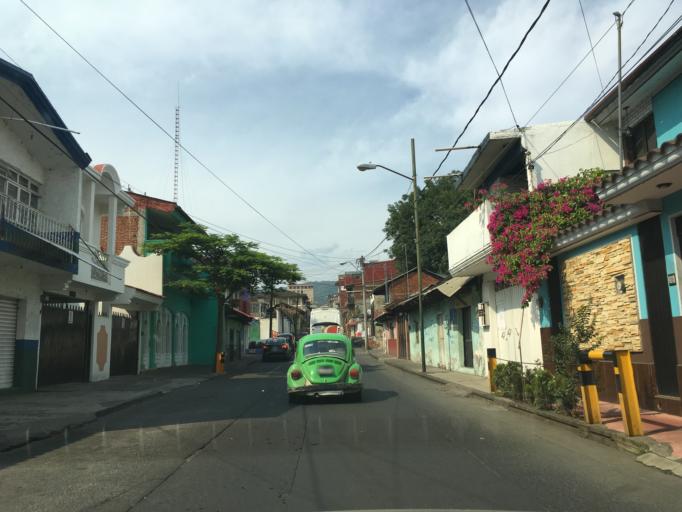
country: MX
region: Michoacan
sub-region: Uruapan
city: Uruapan
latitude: 19.4145
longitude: -102.0637
